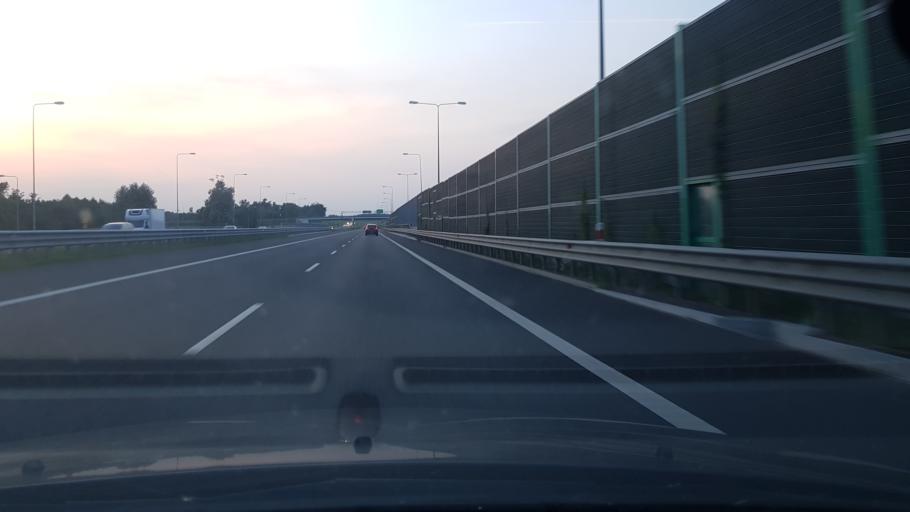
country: PL
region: Warmian-Masurian Voivodeship
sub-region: Powiat olsztynski
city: Olsztynek
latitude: 53.4963
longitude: 20.3153
